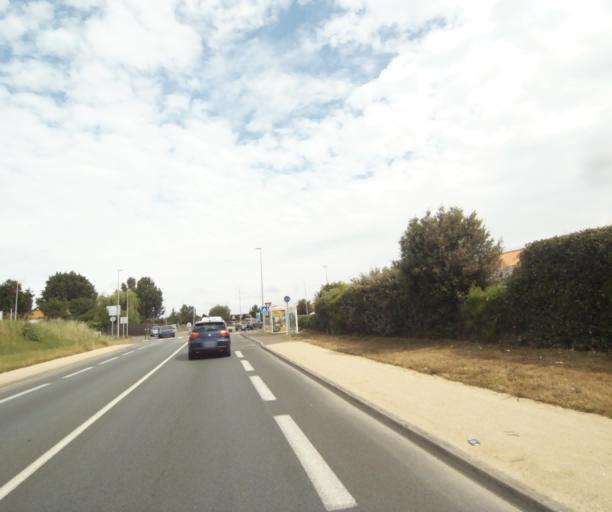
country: FR
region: Pays de la Loire
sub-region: Departement de la Vendee
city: Chateau-d'Olonne
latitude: 46.5013
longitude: -1.7588
